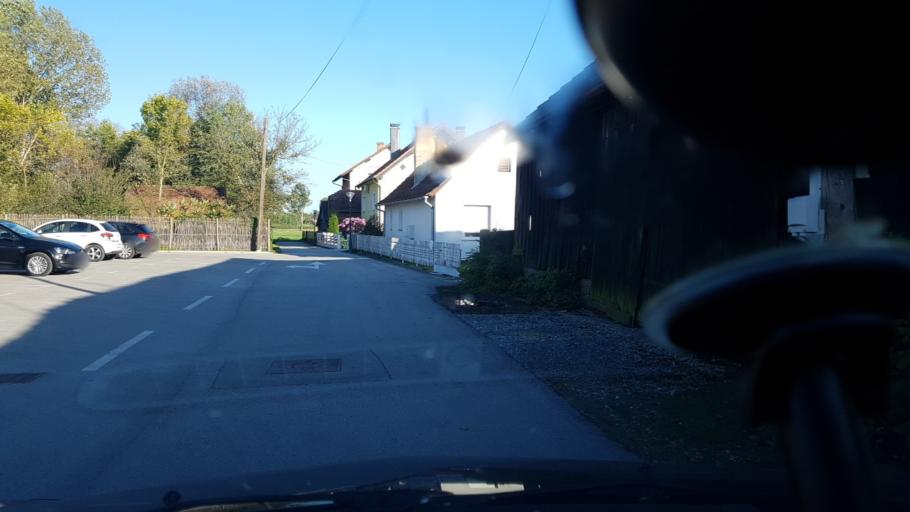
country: HR
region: Koprivnicko-Krizevacka
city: Kalinovac
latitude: 46.0444
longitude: 17.0688
